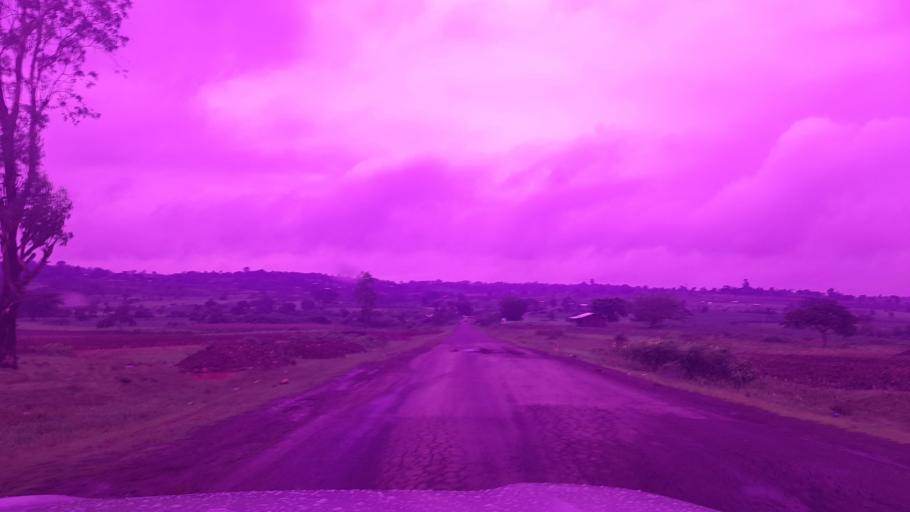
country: ET
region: Oromiya
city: Jima
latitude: 7.6854
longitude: 37.2352
